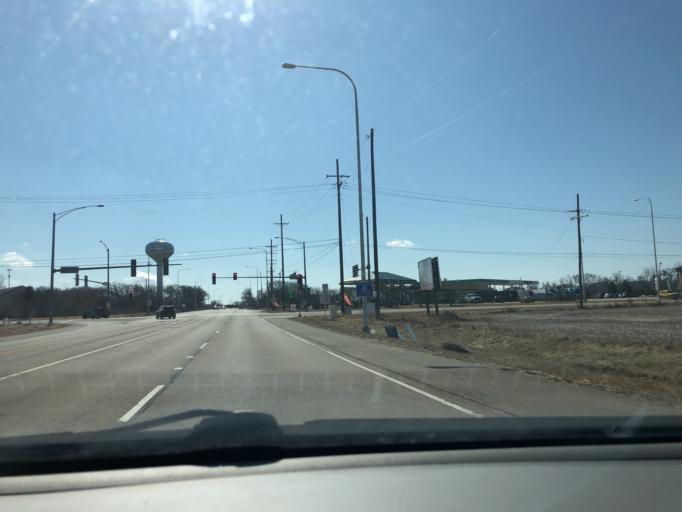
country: US
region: Illinois
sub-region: Kane County
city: Pingree Grove
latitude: 42.0895
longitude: -88.4571
